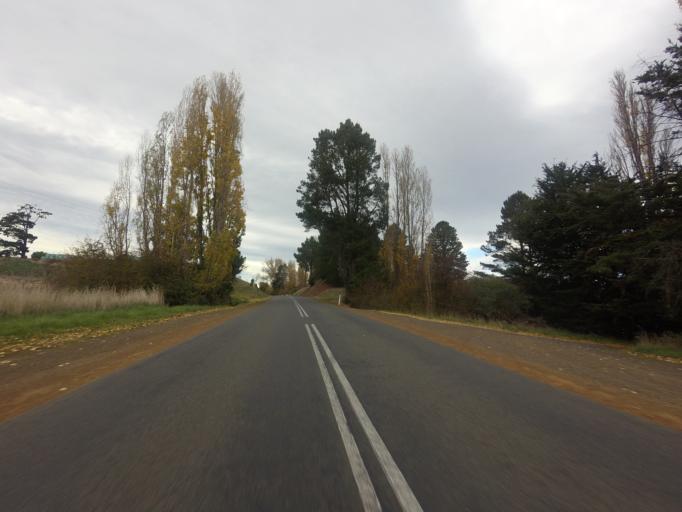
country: AU
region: Tasmania
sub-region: Derwent Valley
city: New Norfolk
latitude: -42.5195
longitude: 146.7486
